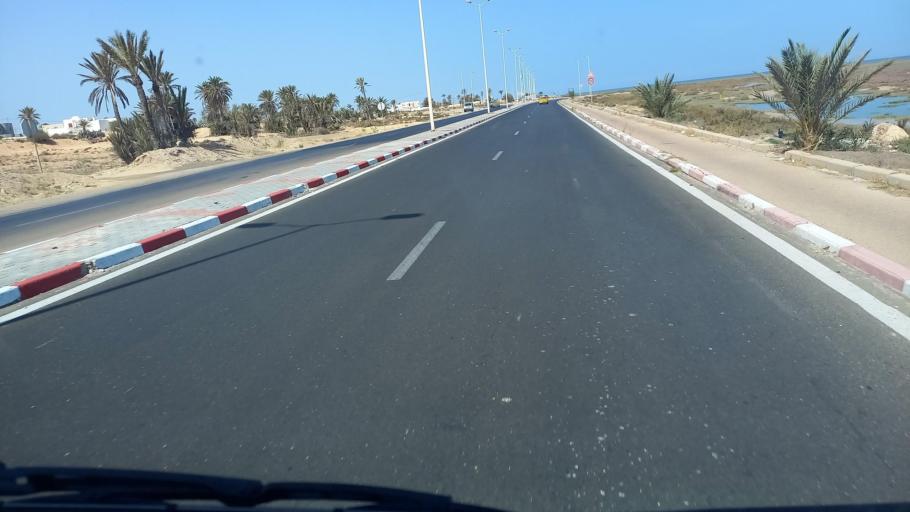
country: TN
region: Madanin
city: Houmt Souk
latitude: 33.8729
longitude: 10.9314
